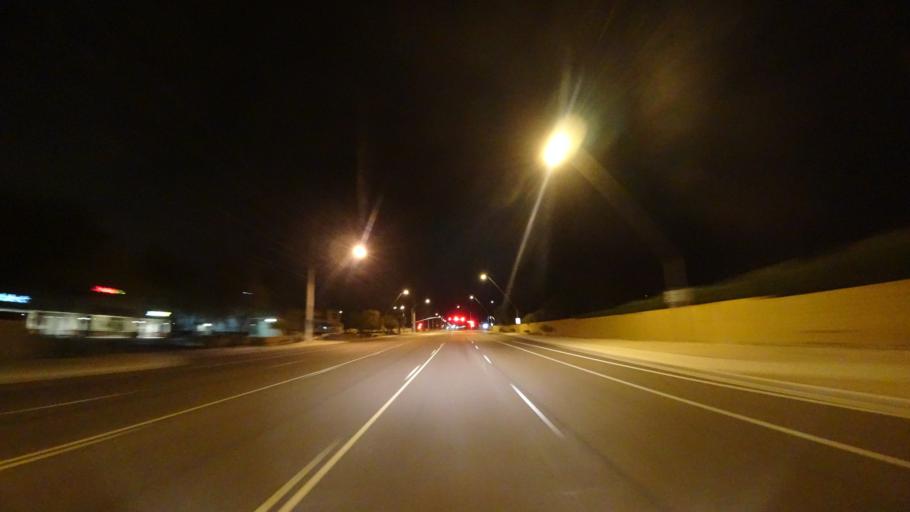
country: US
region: Arizona
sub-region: Pinal County
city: Apache Junction
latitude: 33.4063
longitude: -111.6674
